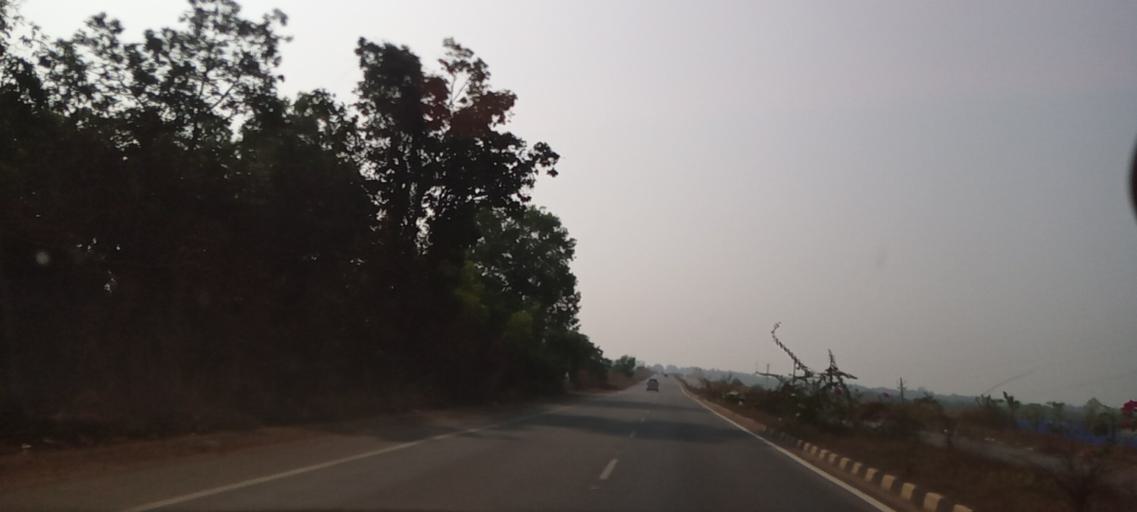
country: IN
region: Karnataka
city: Gangolli
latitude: 13.6672
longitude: 74.7040
